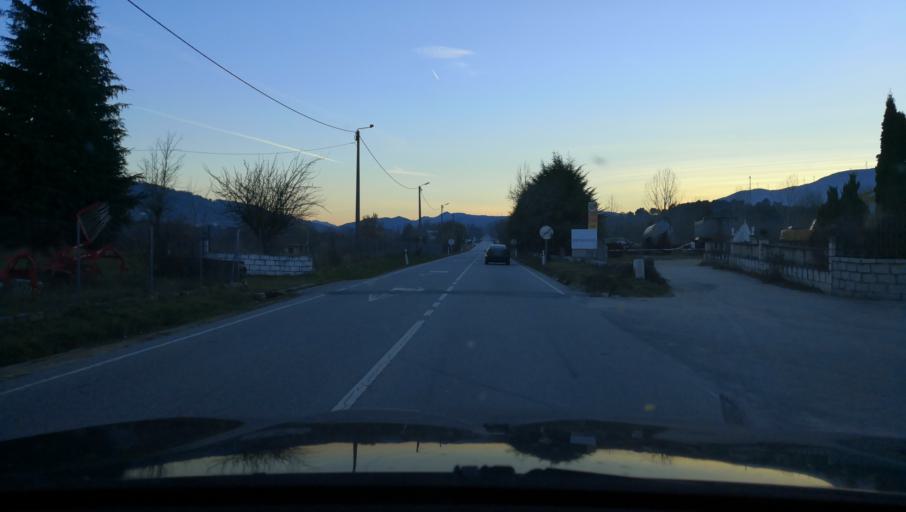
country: PT
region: Vila Real
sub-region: Vila Pouca de Aguiar
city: Vila Pouca de Aguiar
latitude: 41.4381
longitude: -7.6765
